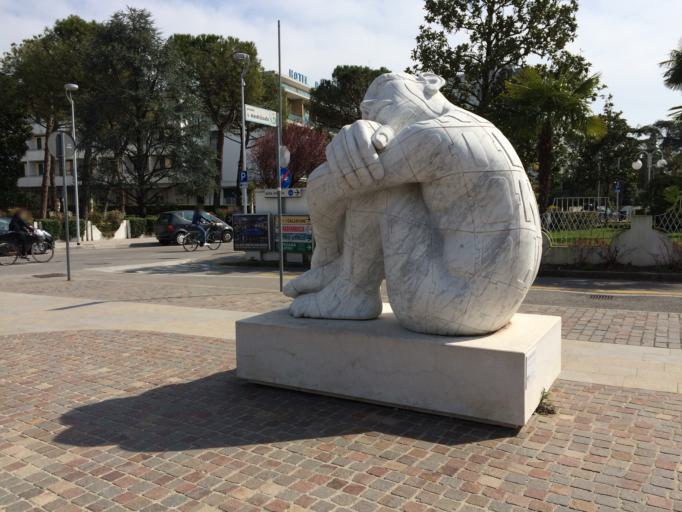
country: IT
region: Veneto
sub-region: Provincia di Padova
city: Abano Terme
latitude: 45.3527
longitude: 11.7858
